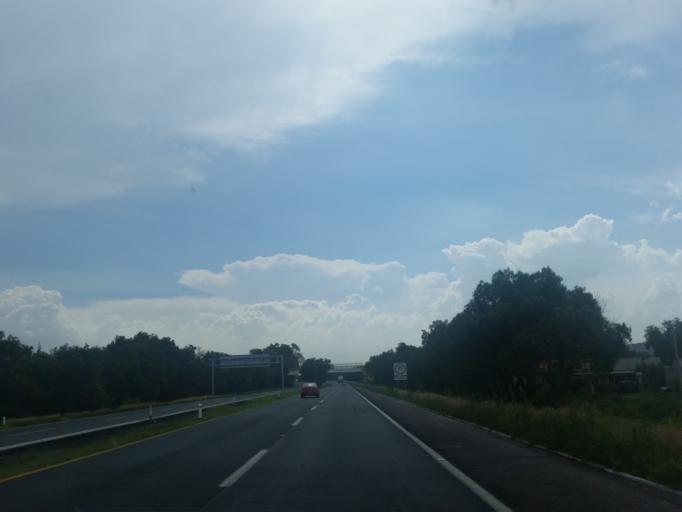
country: MX
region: Mexico
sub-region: Acolman de Nezahualcoyotl
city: Prados de San Juan
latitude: 19.6201
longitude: -98.9569
